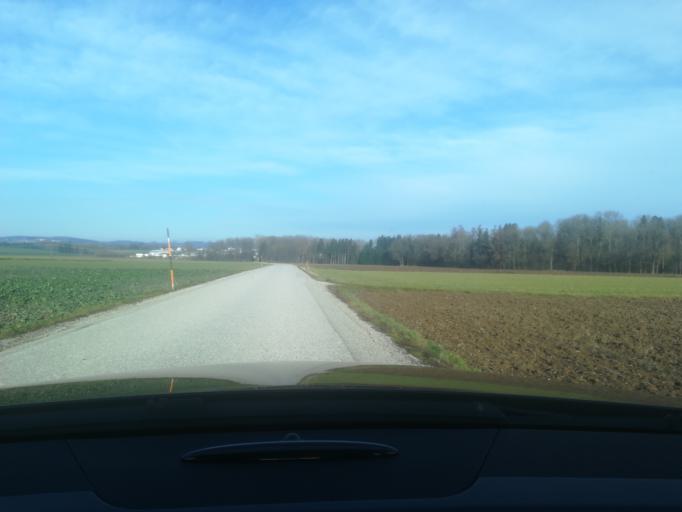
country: AT
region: Upper Austria
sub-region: Wels-Land
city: Holzhausen
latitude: 48.2104
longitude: 14.1018
